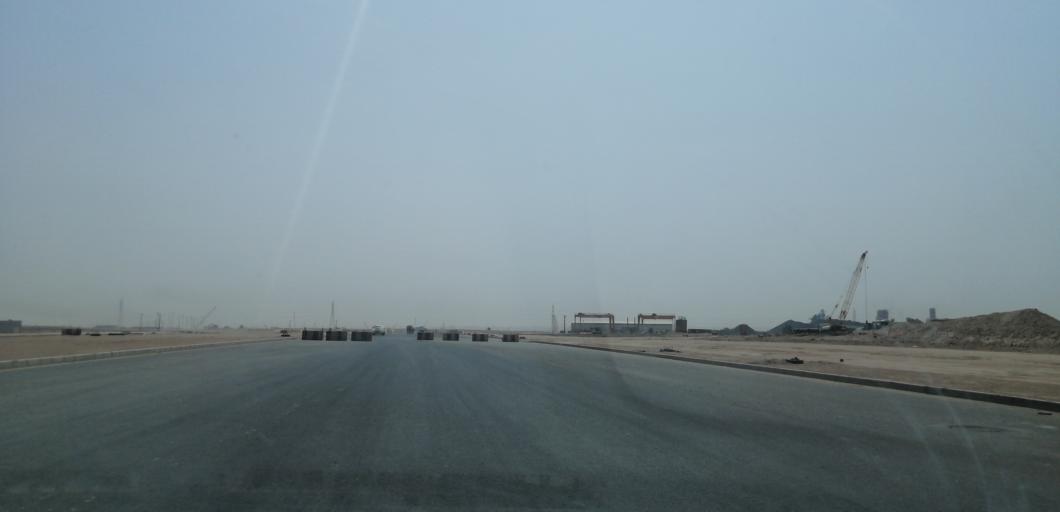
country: KW
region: Muhafazat al Jahra'
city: Al Jahra'
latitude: 29.4465
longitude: 47.6248
